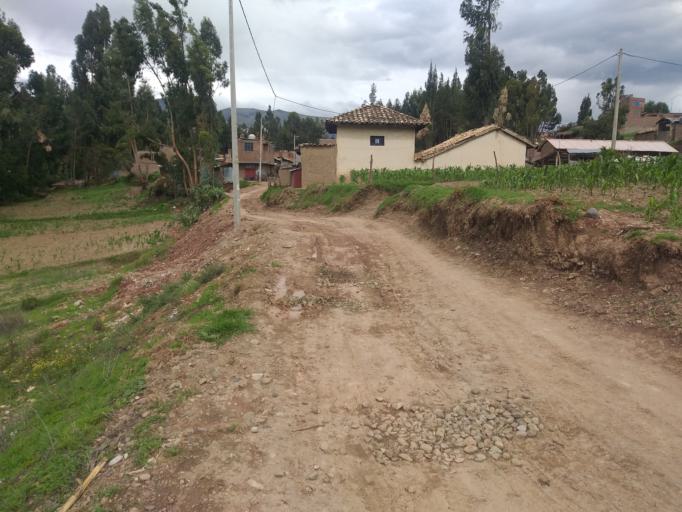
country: PE
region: Junin
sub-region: Provincia de Huancayo
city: Huayucachi
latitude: -12.1162
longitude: -75.2219
